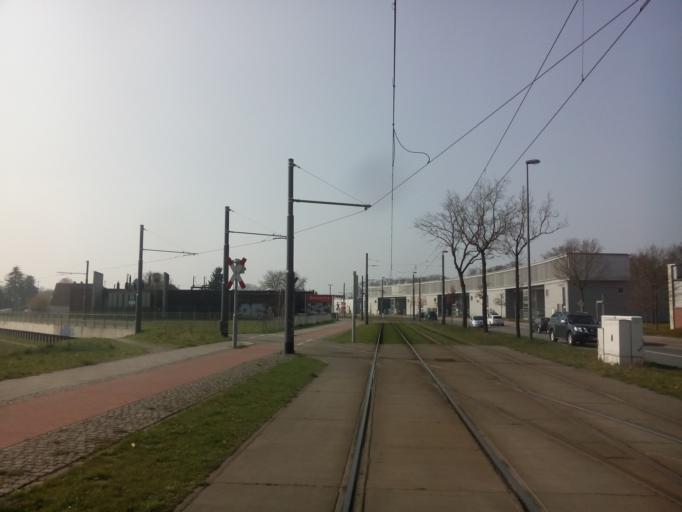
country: DE
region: Lower Saxony
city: Oyten
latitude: 53.0606
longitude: 8.9634
